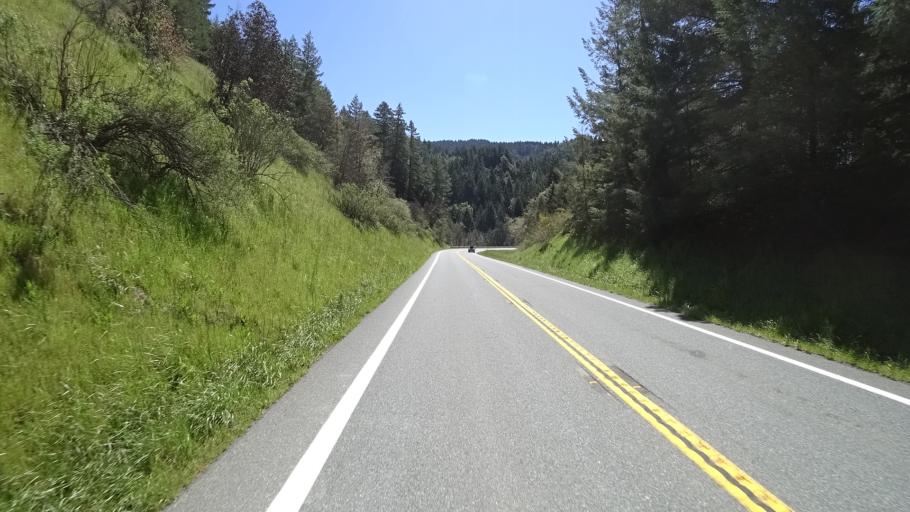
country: US
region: California
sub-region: Humboldt County
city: Willow Creek
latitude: 40.9051
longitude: -123.8056
